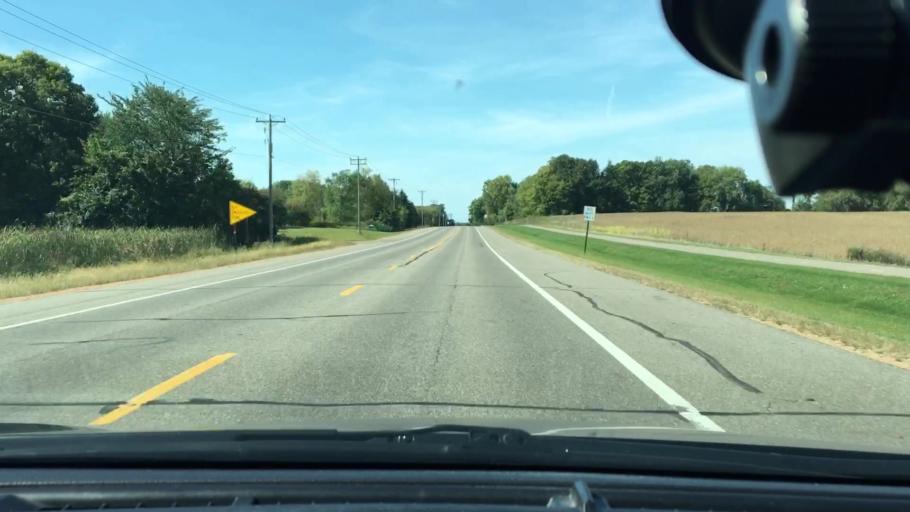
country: US
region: Minnesota
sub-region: Wright County
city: Hanover
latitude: 45.1525
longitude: -93.6528
